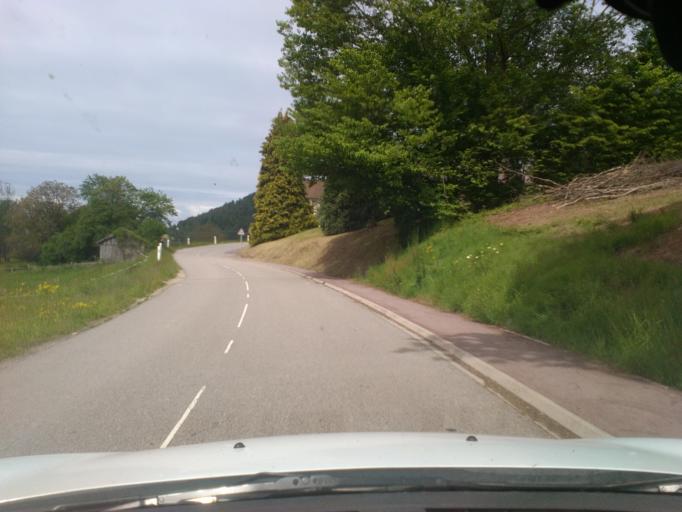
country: FR
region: Lorraine
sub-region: Departement des Vosges
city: Le Tholy
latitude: 48.1369
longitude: 6.7014
